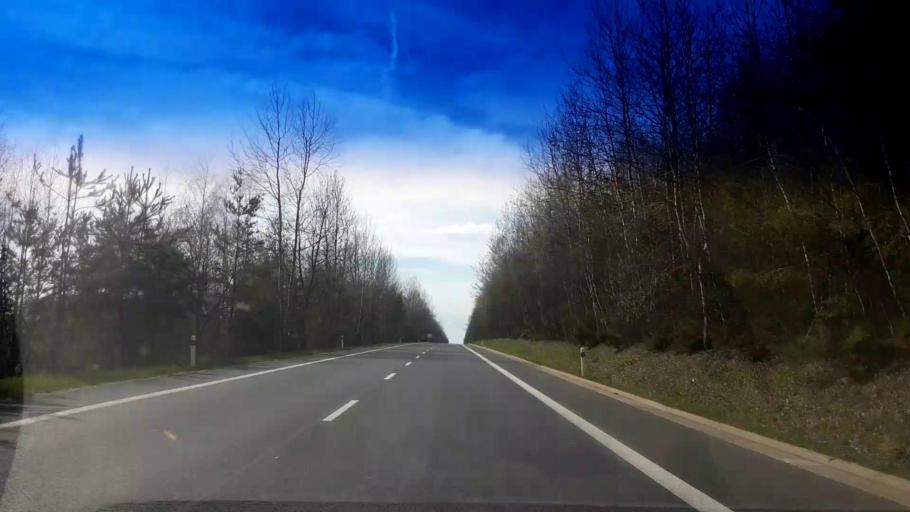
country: CZ
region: Karlovarsky
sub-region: Okres Cheb
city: Frantiskovy Lazne
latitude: 50.0980
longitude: 12.3119
